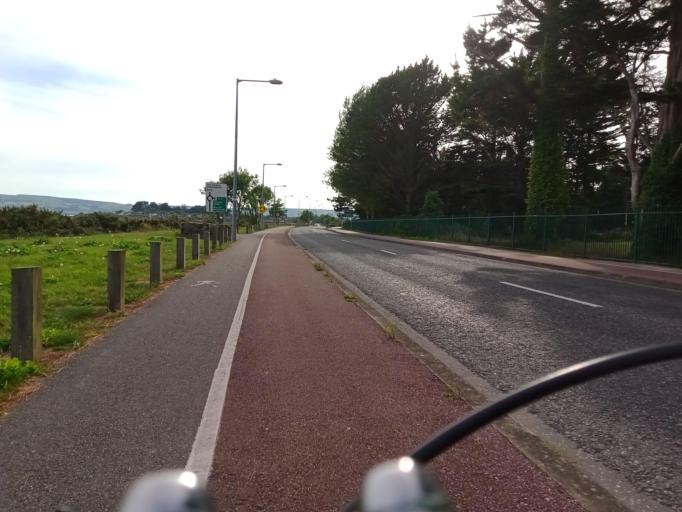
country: IE
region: Munster
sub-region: Waterford
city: Dungarvan
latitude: 52.0999
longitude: -7.5883
